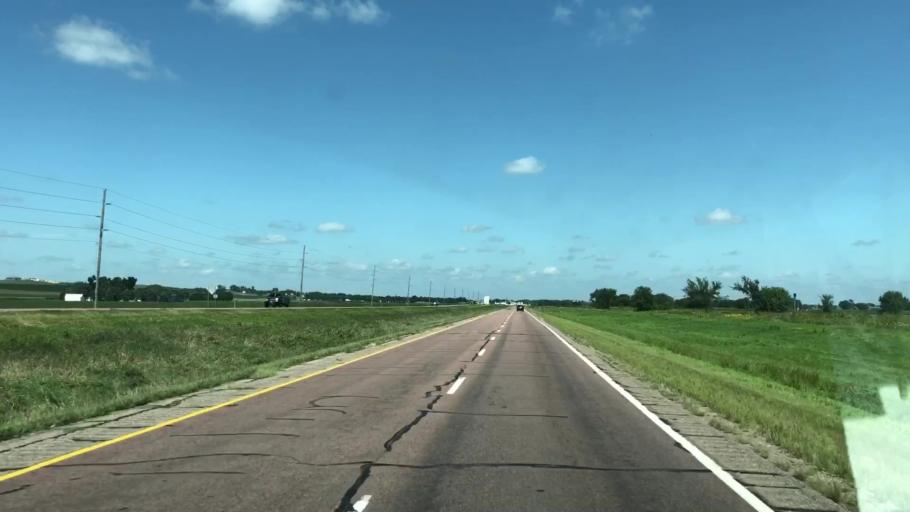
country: US
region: Iowa
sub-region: Plymouth County
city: Le Mars
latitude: 42.6931
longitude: -96.2616
